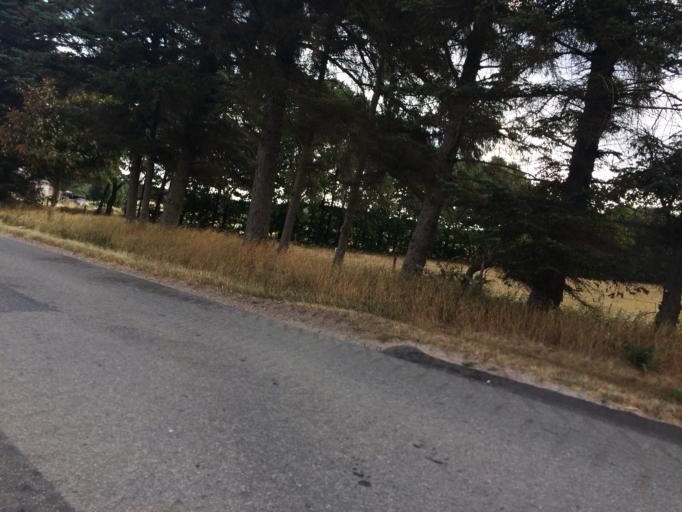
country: DK
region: Central Jutland
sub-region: Holstebro Kommune
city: Vinderup
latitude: 56.6149
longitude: 8.7331
